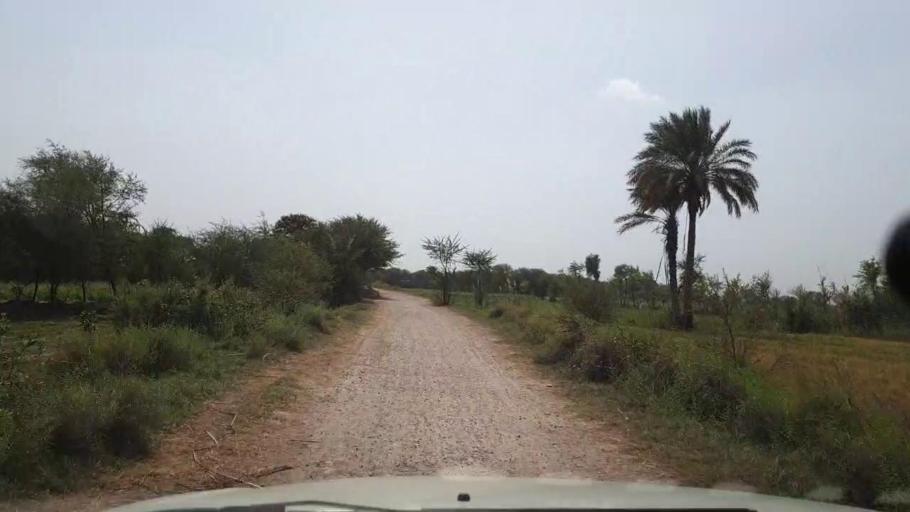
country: PK
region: Sindh
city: Matli
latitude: 25.0225
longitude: 68.7114
